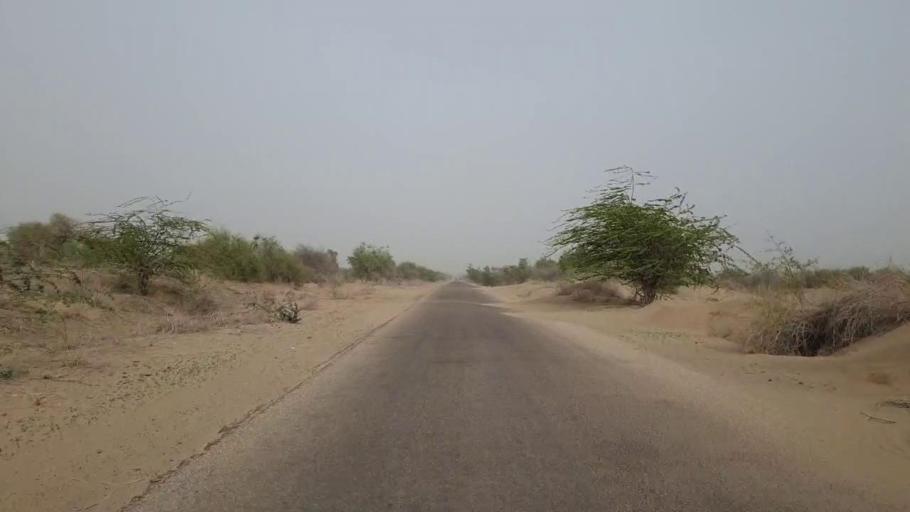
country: PK
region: Sindh
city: Islamkot
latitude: 24.5778
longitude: 70.3087
